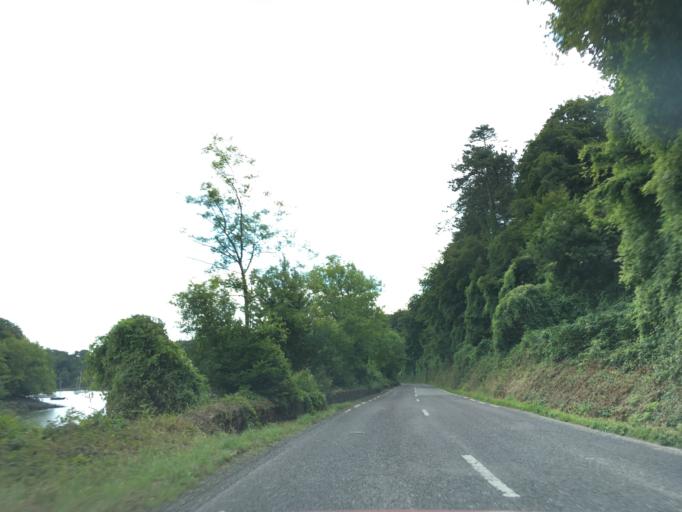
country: IE
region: Munster
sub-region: County Cork
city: Crosshaven
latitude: 51.8060
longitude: -8.3408
